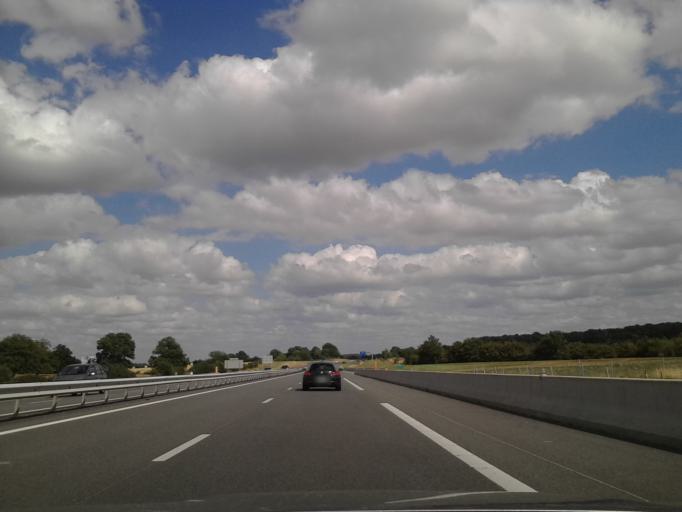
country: FR
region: Centre
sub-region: Departement du Cher
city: Orval
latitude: 46.7229
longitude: 2.4429
